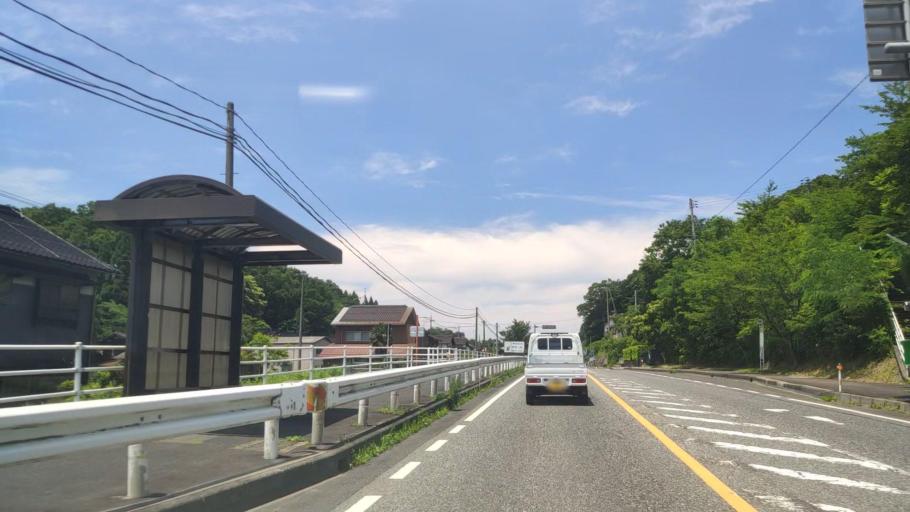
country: JP
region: Tottori
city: Tottori
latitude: 35.4281
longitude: 134.2605
